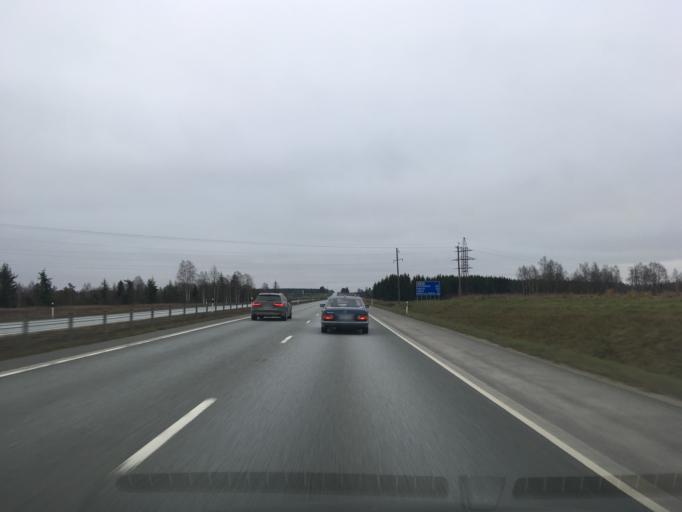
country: EE
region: Laeaene-Virumaa
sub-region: Haljala vald
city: Haljala
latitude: 59.4226
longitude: 26.2812
